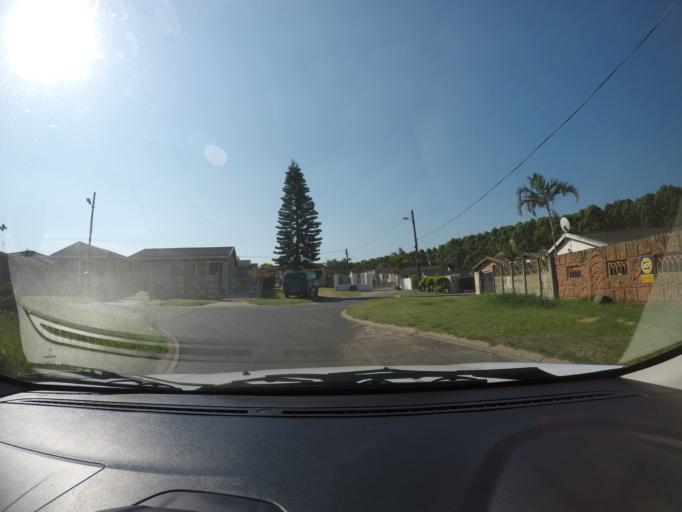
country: ZA
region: KwaZulu-Natal
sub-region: uThungulu District Municipality
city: Richards Bay
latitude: -28.7164
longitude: 32.0440
